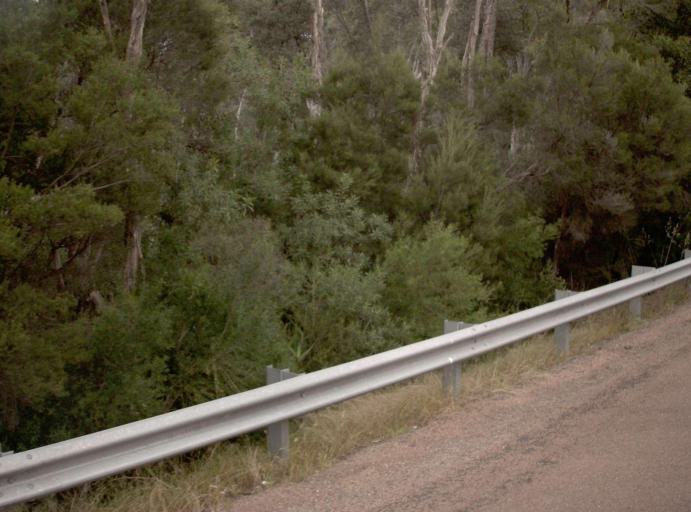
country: AU
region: Victoria
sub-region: East Gippsland
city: Bairnsdale
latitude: -37.8893
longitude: 147.6594
